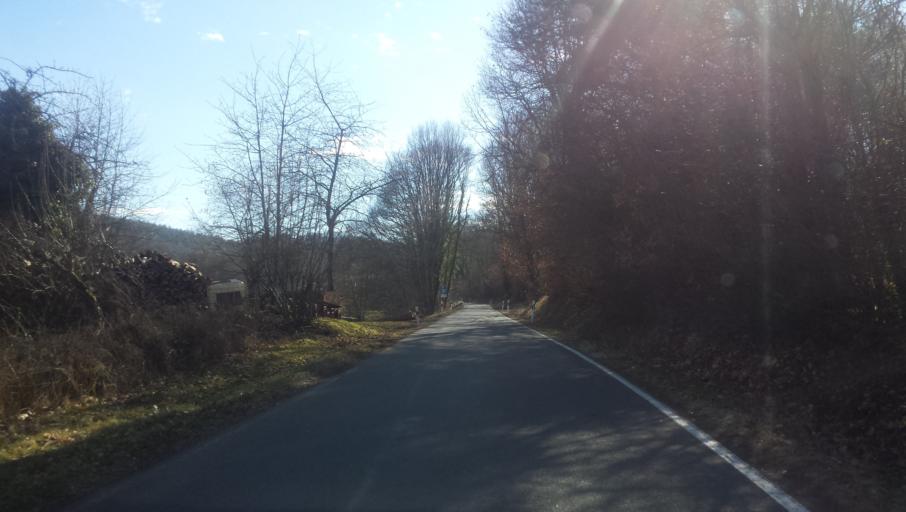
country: DE
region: Hesse
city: Gross-Bieberau
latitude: 49.7671
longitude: 8.8165
